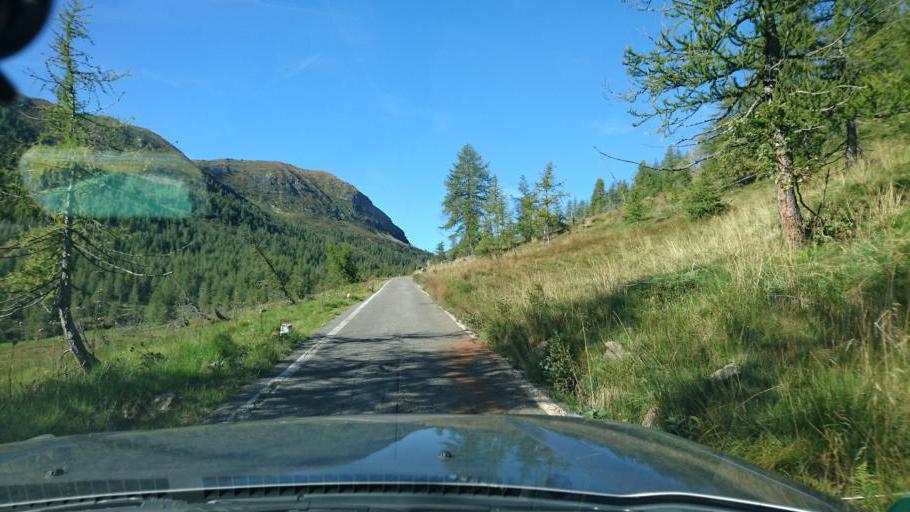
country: IT
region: Lombardy
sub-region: Provincia di Bergamo
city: Schilpario
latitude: 46.0407
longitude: 10.2150
